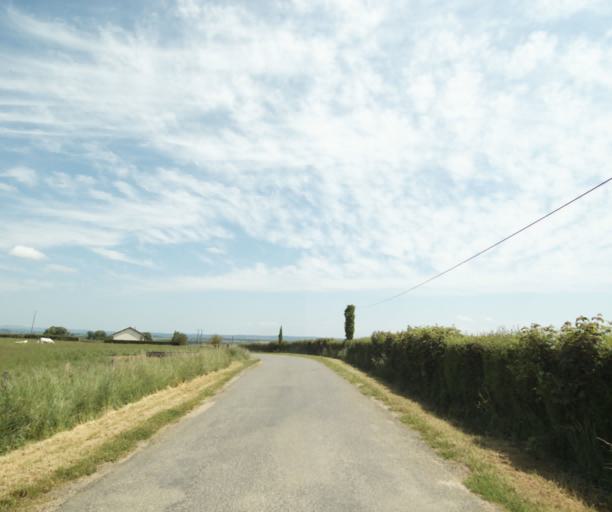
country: FR
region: Bourgogne
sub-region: Departement de Saone-et-Loire
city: Perrecy-les-Forges
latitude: 46.5980
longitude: 4.1439
